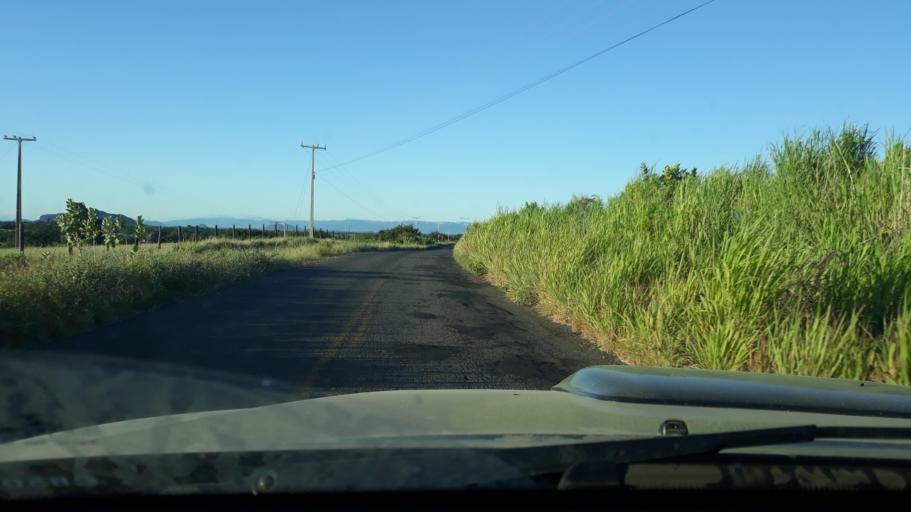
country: BR
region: Bahia
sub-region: Guanambi
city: Guanambi
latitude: -14.0572
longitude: -42.8754
